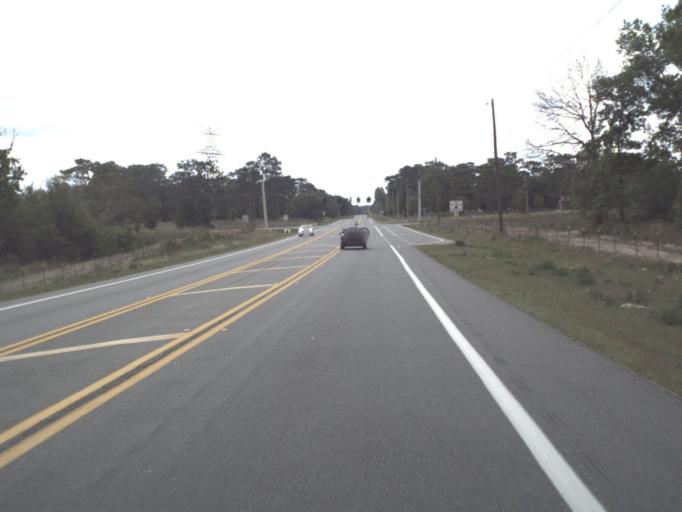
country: US
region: Florida
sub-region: Marion County
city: Ocala
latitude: 29.2429
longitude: -82.0556
